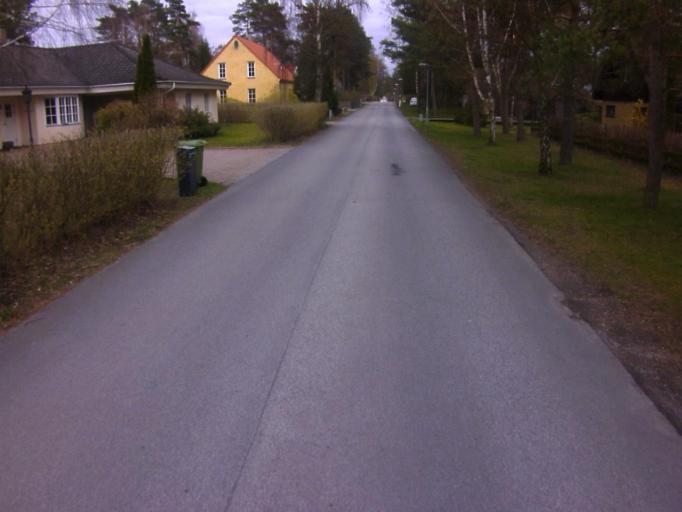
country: SE
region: Skane
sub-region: Kavlinge Kommun
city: Hofterup
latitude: 55.7947
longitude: 12.9705
